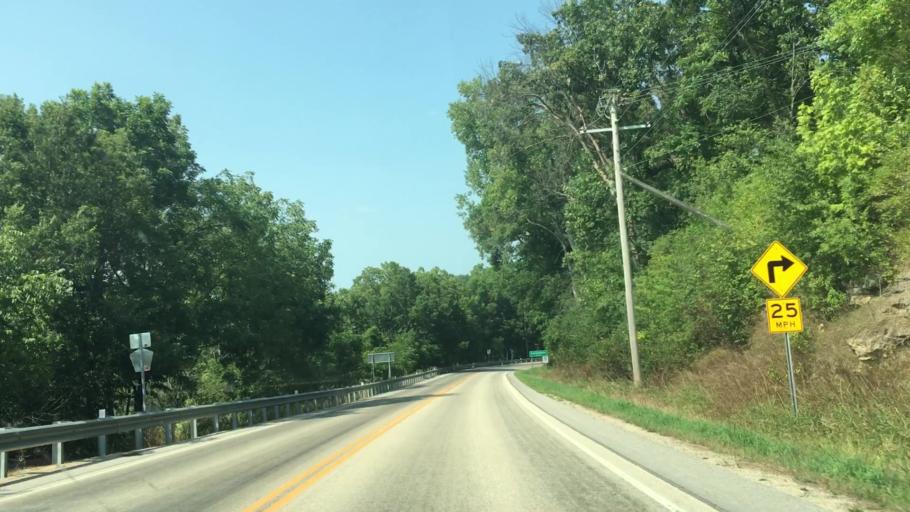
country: US
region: Minnesota
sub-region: Fillmore County
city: Preston
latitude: 43.7124
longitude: -91.9813
